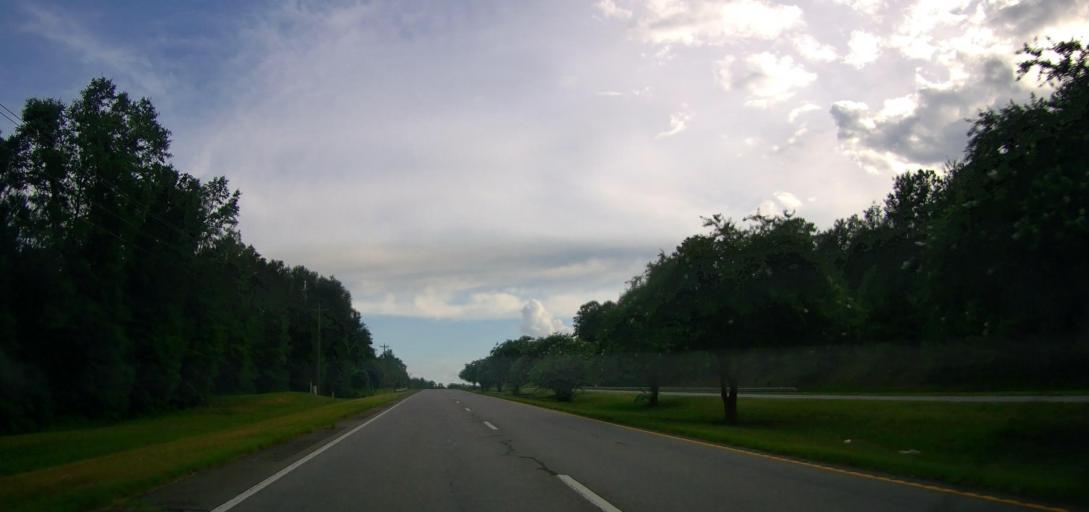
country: US
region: Georgia
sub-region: Peach County
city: Byron
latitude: 32.6181
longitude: -83.7889
